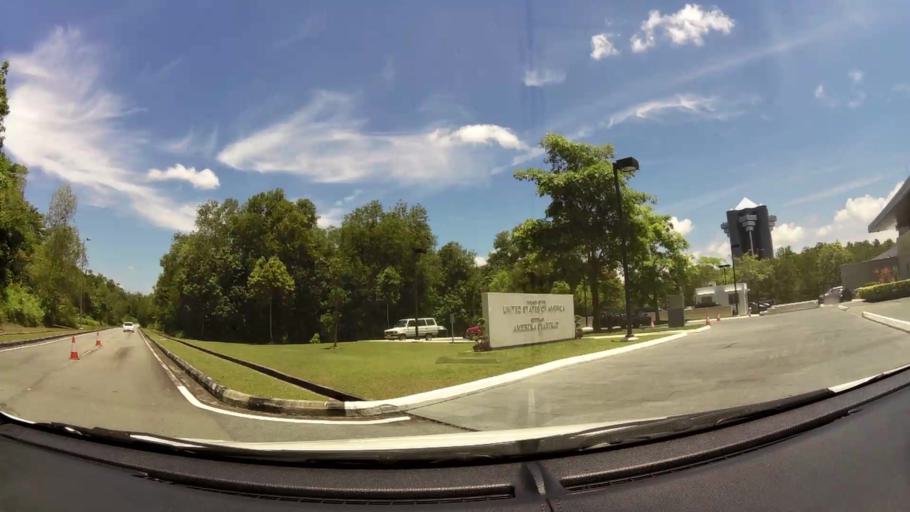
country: BN
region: Brunei and Muara
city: Bandar Seri Begawan
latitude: 4.9194
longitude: 114.9564
